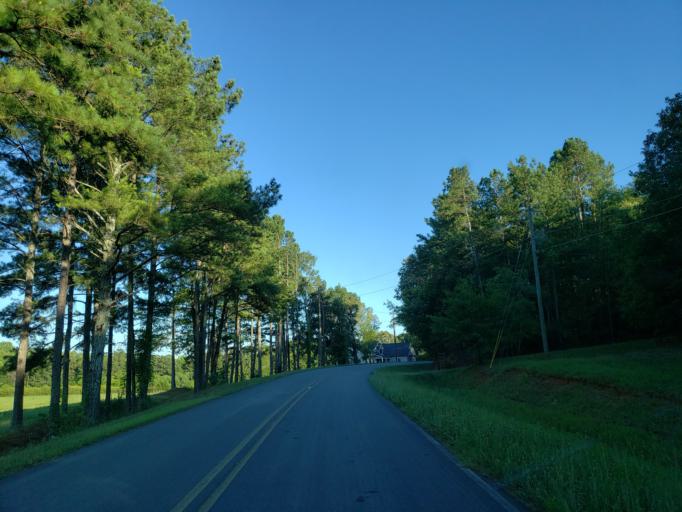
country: US
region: Georgia
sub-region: Bartow County
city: Euharlee
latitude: 34.1021
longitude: -84.9985
